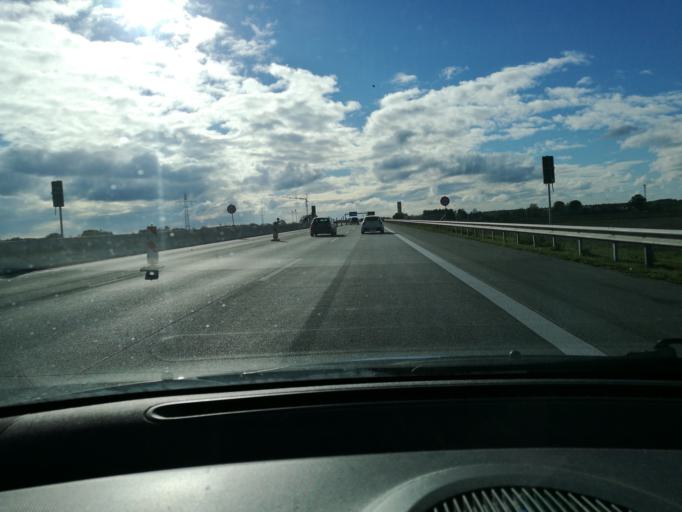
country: DE
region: Schleswig-Holstein
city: Wasbek
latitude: 54.0827
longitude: 9.9260
